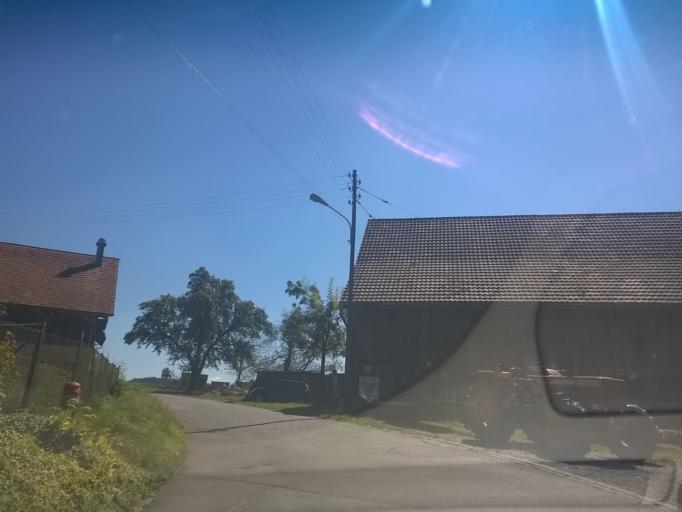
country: CH
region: Zurich
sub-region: Bezirk Winterthur
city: Pfungen
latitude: 47.4863
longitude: 8.6393
